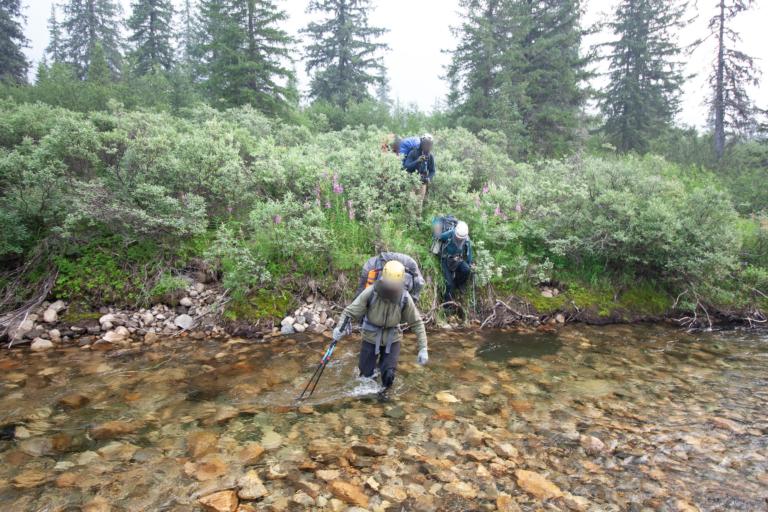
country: RU
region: Respublika Buryatiya
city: Kichera
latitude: 56.2401
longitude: 110.5415
